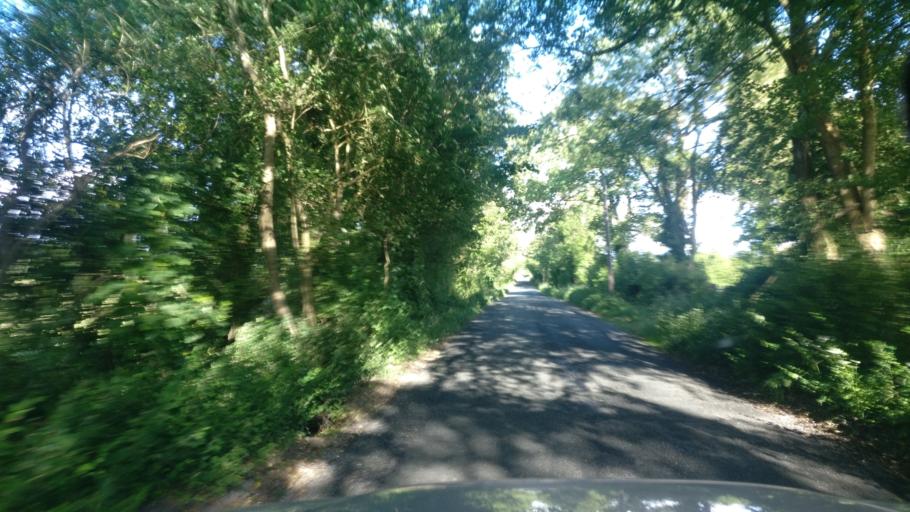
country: IE
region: Connaught
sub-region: County Galway
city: Ballinasloe
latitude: 53.2296
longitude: -8.2451
